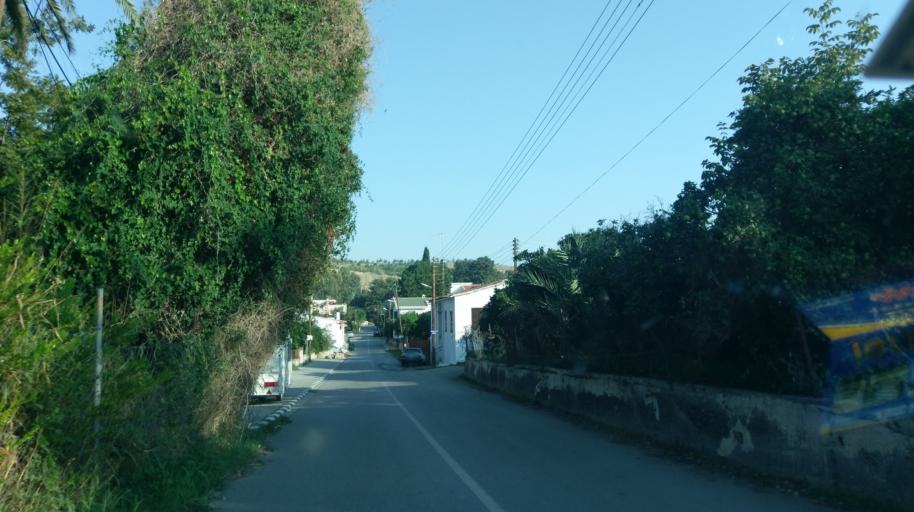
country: CY
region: Lefkosia
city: Lefka
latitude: 35.1169
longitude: 32.8529
